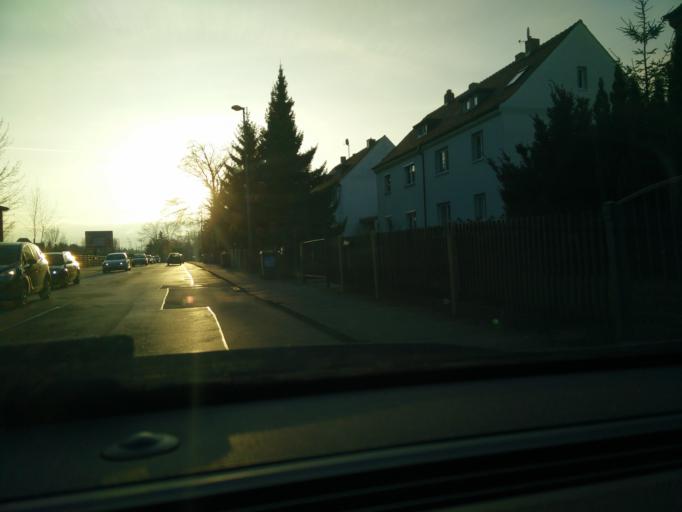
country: DE
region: Saxony
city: Taucha
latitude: 51.3298
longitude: 12.4399
